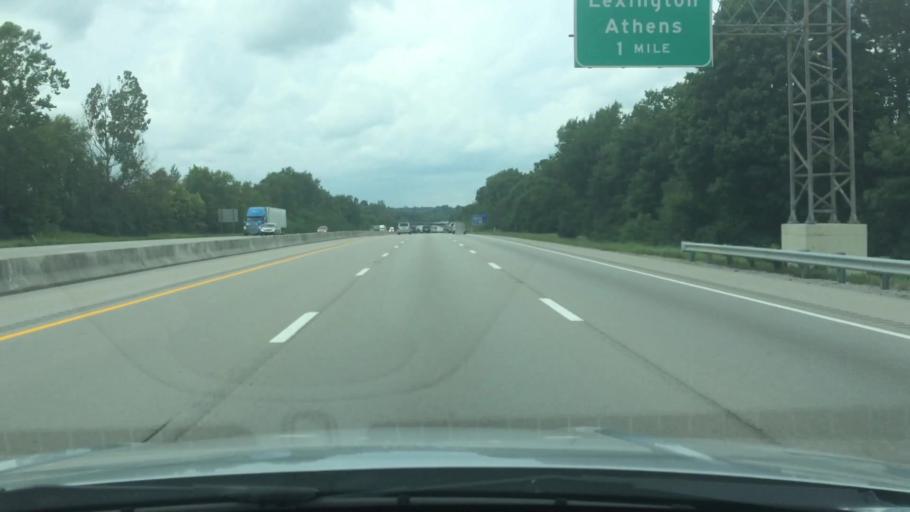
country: US
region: Kentucky
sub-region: Fayette County
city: Lexington
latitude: 37.9432
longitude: -84.3818
